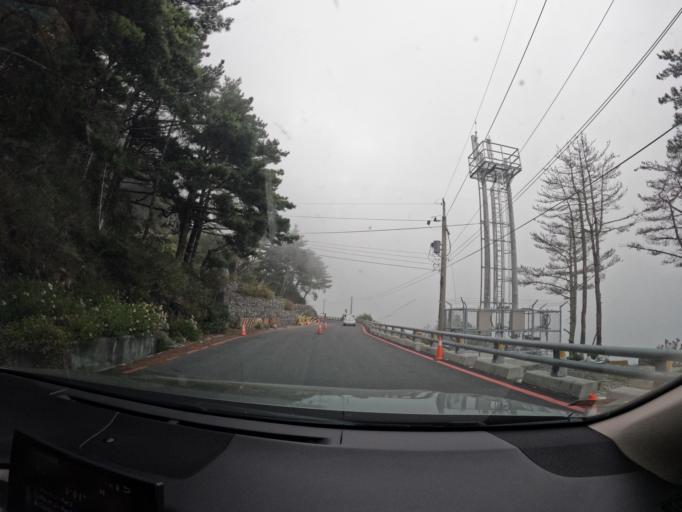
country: TW
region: Taiwan
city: Yujing
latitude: 23.2647
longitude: 120.9660
